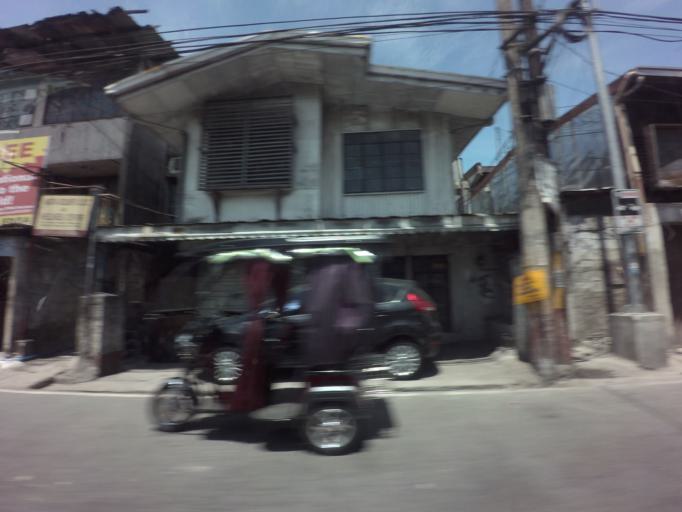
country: PH
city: Sambayanihan People's Village
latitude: 14.5070
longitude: 120.9943
